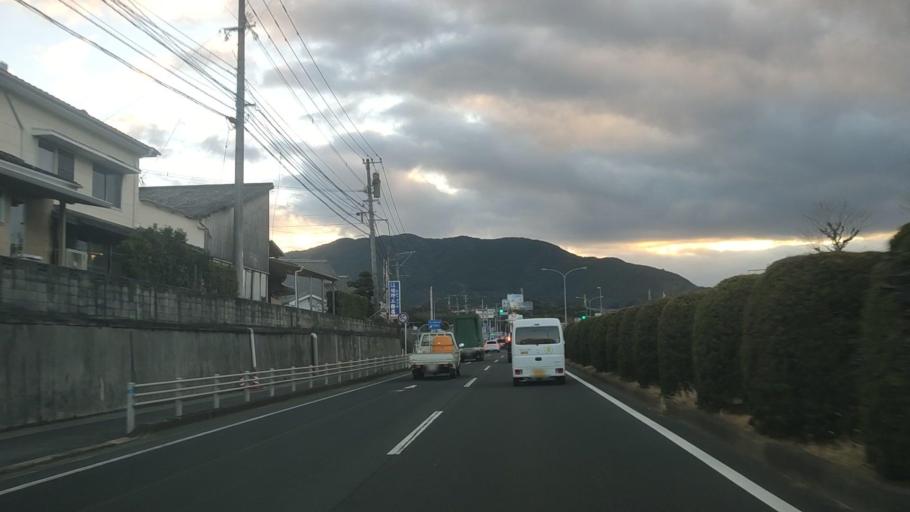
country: JP
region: Nagasaki
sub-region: Isahaya-shi
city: Isahaya
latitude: 32.8344
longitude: 130.0032
